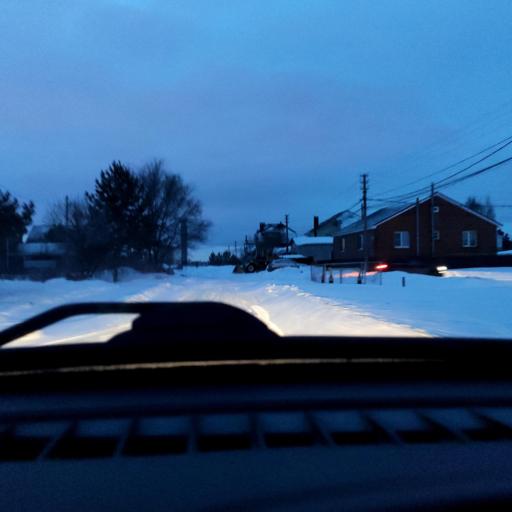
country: RU
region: Samara
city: Tol'yatti
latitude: 53.5529
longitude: 49.3743
